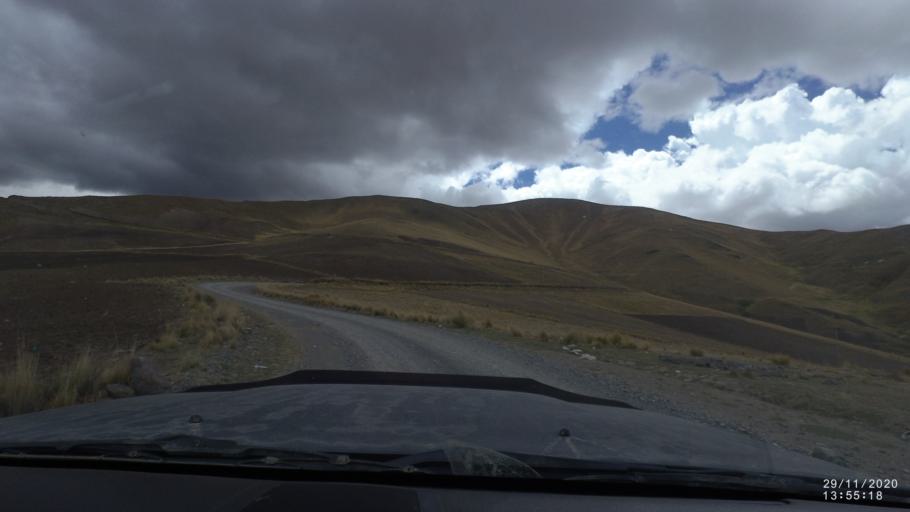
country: BO
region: Cochabamba
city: Sipe Sipe
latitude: -17.1751
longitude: -66.3565
